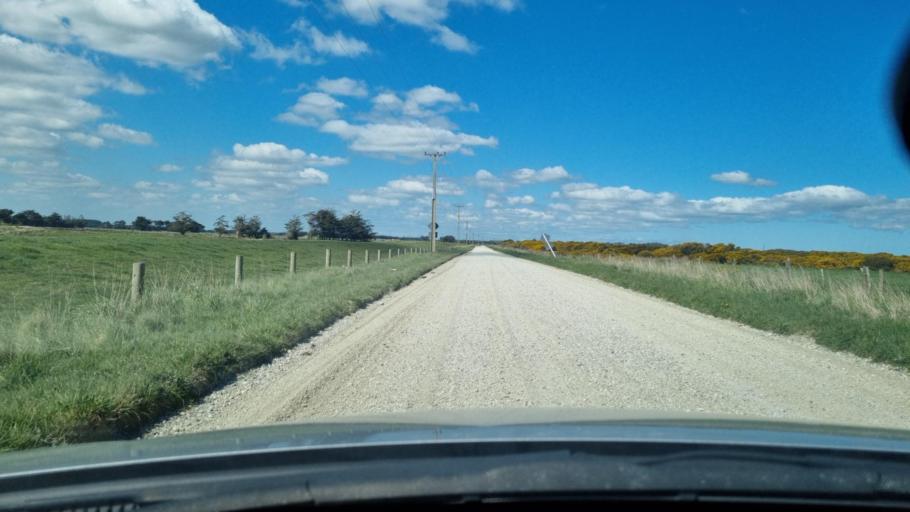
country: NZ
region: Southland
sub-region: Invercargill City
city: Invercargill
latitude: -46.3915
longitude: 168.2647
